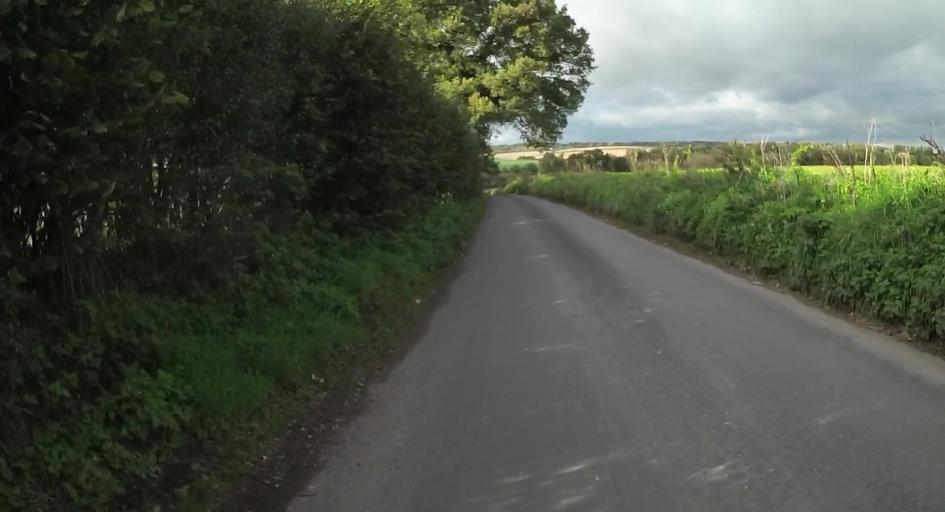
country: GB
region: England
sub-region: Hampshire
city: Alton
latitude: 51.1648
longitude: -0.9263
